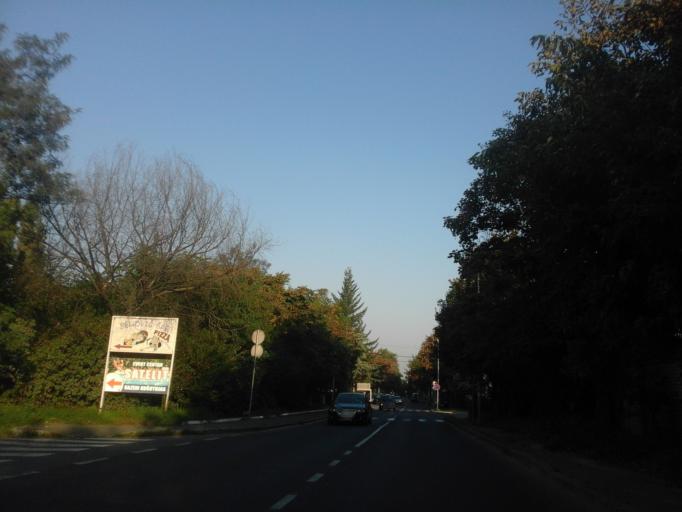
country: RS
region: Central Serbia
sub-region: Belgrade
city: Cukarica
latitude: 44.7665
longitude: 20.4236
